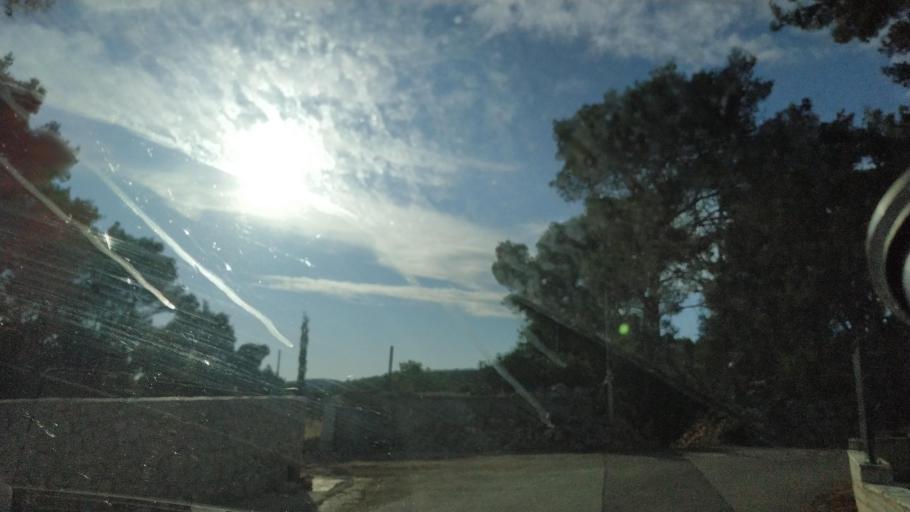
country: HR
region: Splitsko-Dalmatinska
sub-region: Grad Trogir
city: Trogir
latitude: 43.4836
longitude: 16.2445
